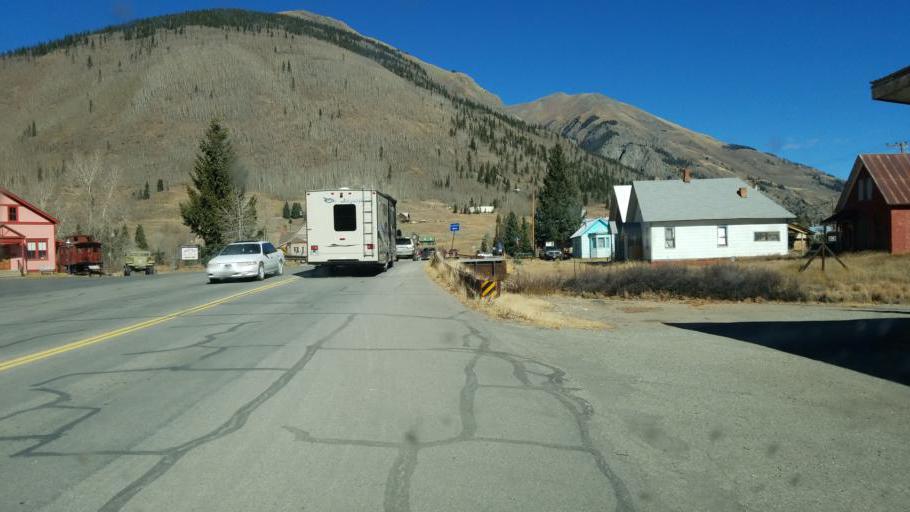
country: US
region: Colorado
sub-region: San Juan County
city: Silverton
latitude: 37.8144
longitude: -107.6617
